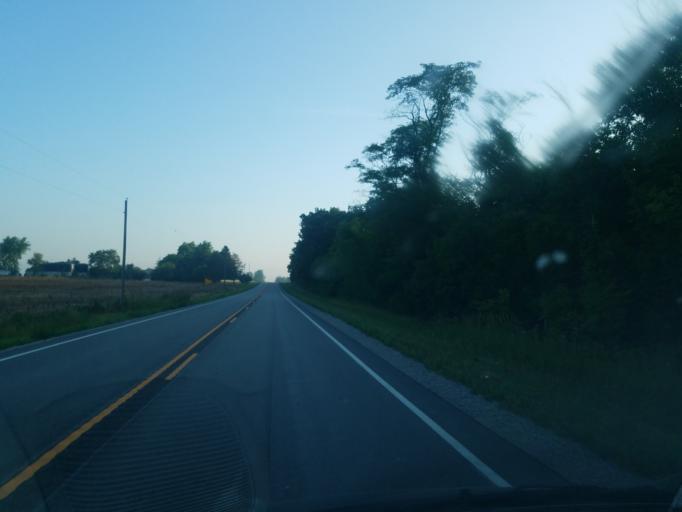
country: US
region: Indiana
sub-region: Allen County
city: Harlan
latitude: 41.2381
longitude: -84.8658
